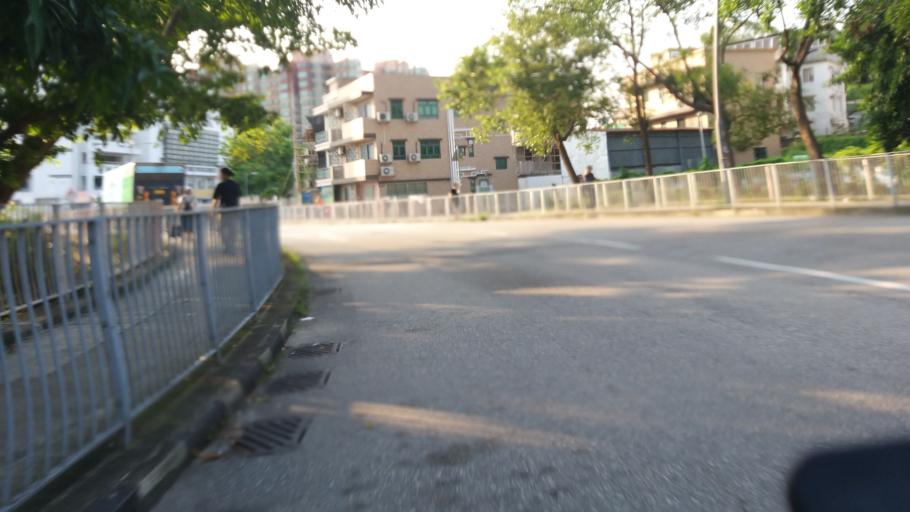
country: HK
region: Yuen Long
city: Yuen Long Kau Hui
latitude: 22.4479
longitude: 114.0341
